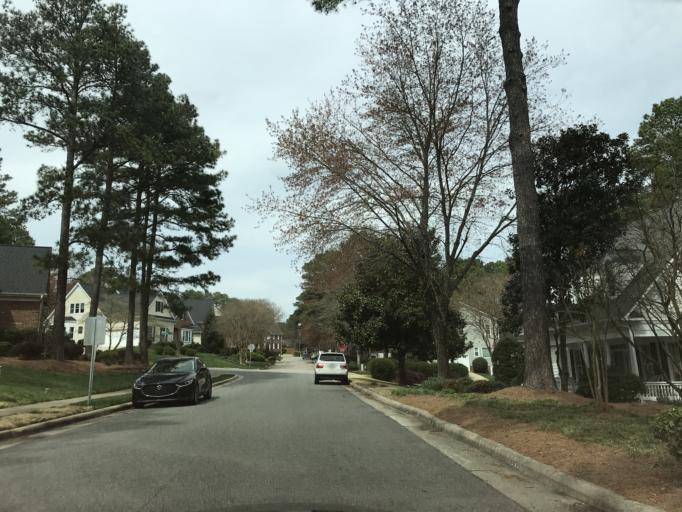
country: US
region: North Carolina
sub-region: Wake County
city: West Raleigh
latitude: 35.8853
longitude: -78.6851
